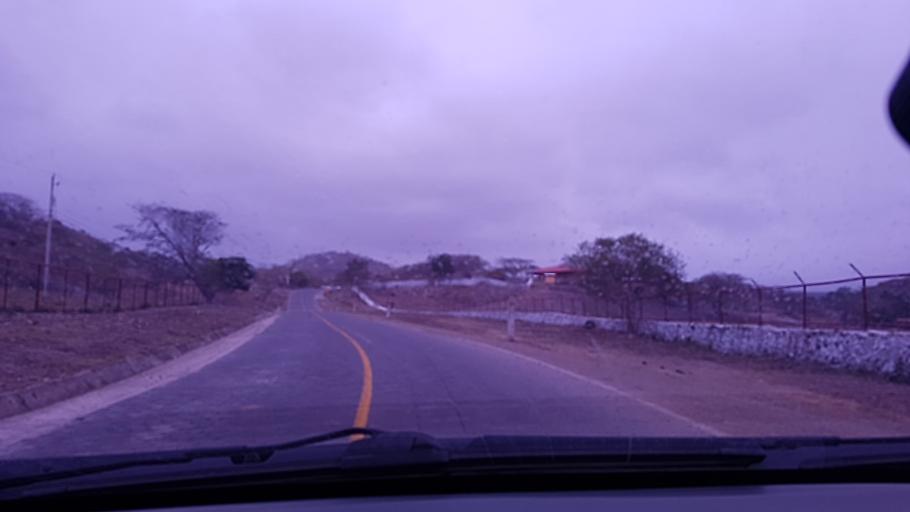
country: NI
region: Jinotega
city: La Concordia
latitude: 13.1617
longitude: -86.1724
